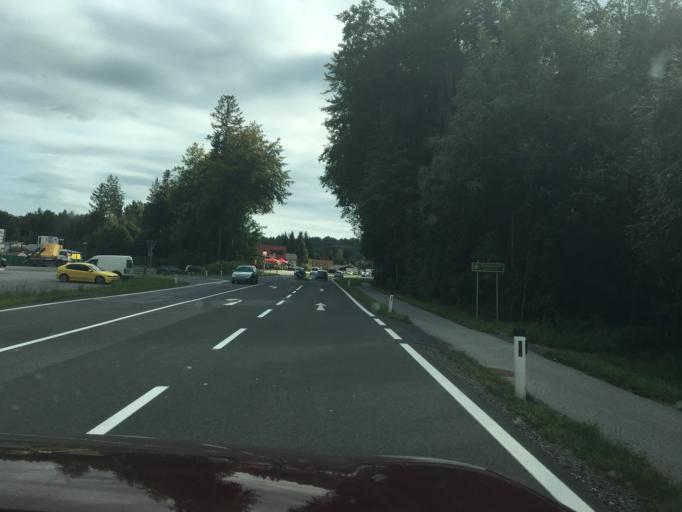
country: AT
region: Styria
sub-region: Politischer Bezirk Deutschlandsberg
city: Deutschlandsberg
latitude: 46.8028
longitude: 15.2220
